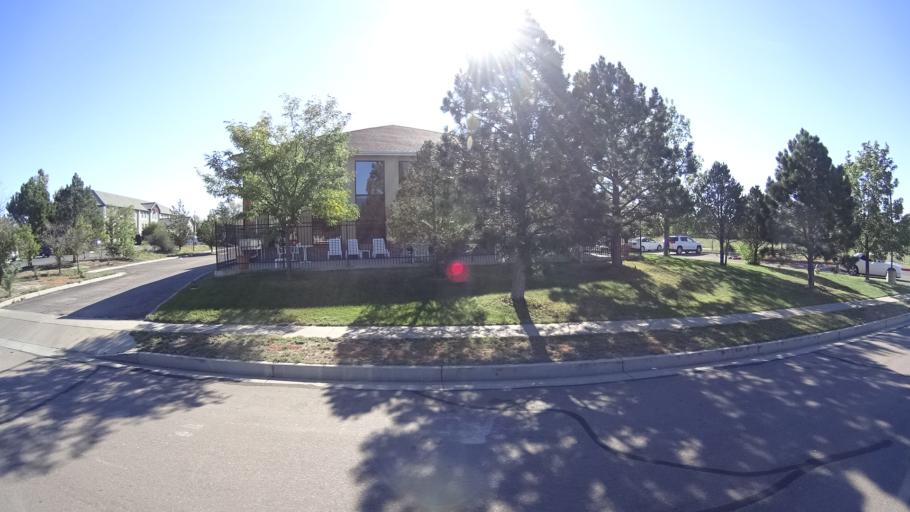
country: US
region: Colorado
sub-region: El Paso County
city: Stratmoor
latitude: 38.8000
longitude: -104.7328
